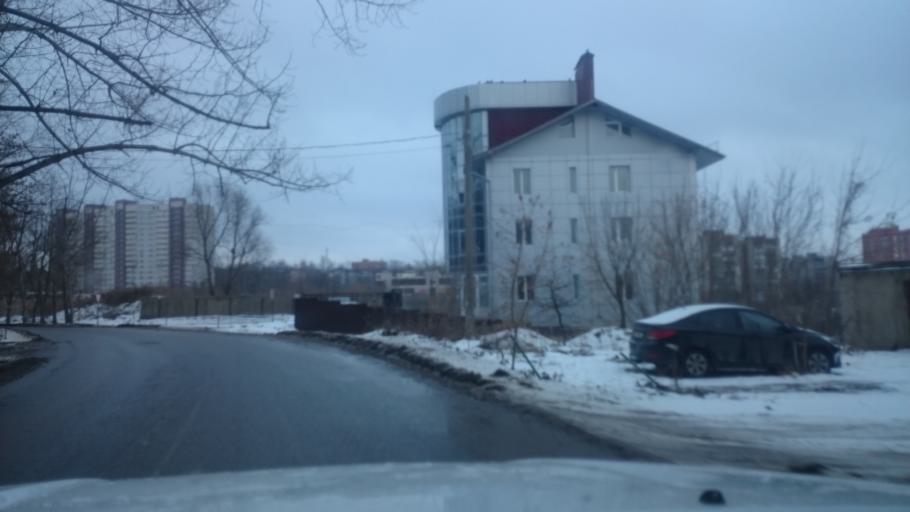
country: RU
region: Tula
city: Mendeleyevskiy
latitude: 54.1710
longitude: 37.5657
